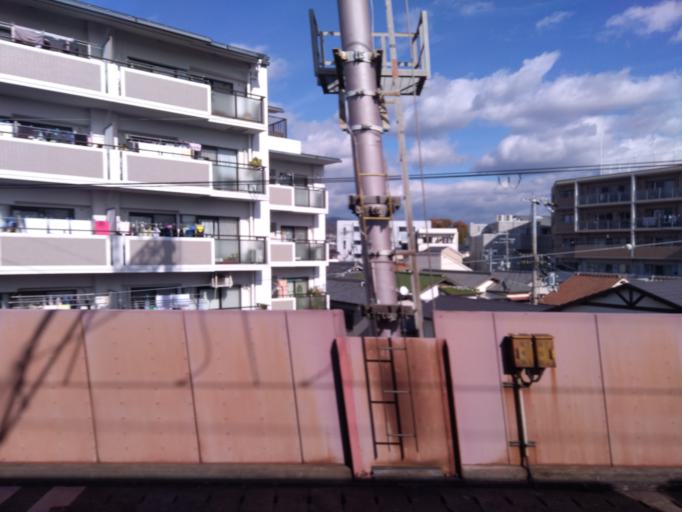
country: JP
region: Osaka
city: Ikeda
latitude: 34.8112
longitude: 135.4418
